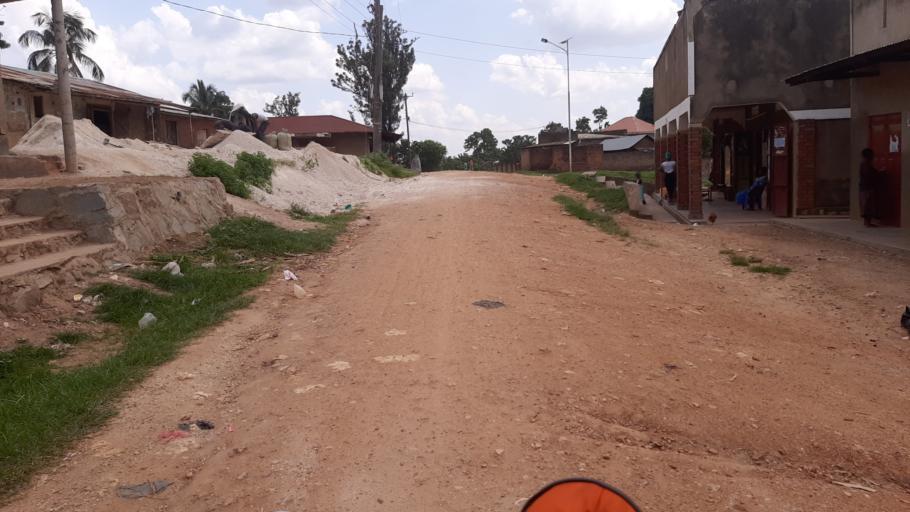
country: UG
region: Eastern Region
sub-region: Mbale District
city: Mbale
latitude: 1.0609
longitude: 34.2069
